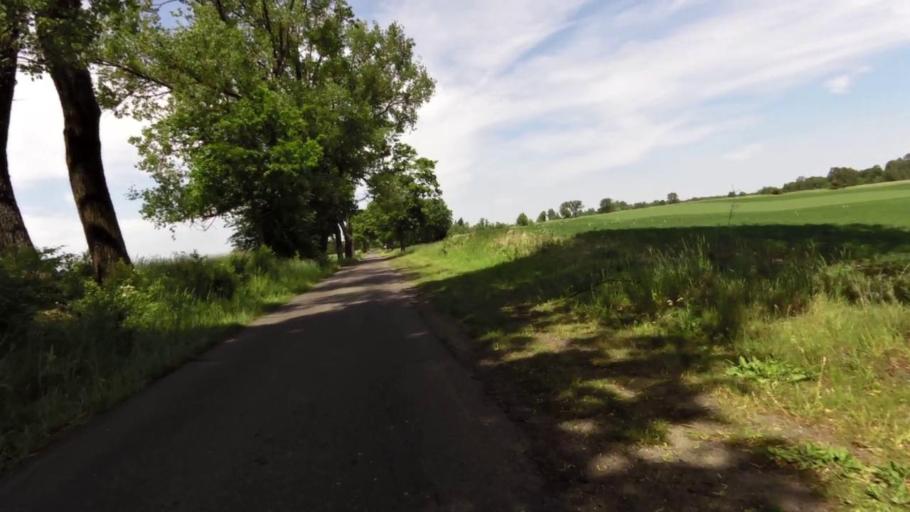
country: PL
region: West Pomeranian Voivodeship
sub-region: Powiat szczecinecki
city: Szczecinek
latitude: 53.6379
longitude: 16.6841
